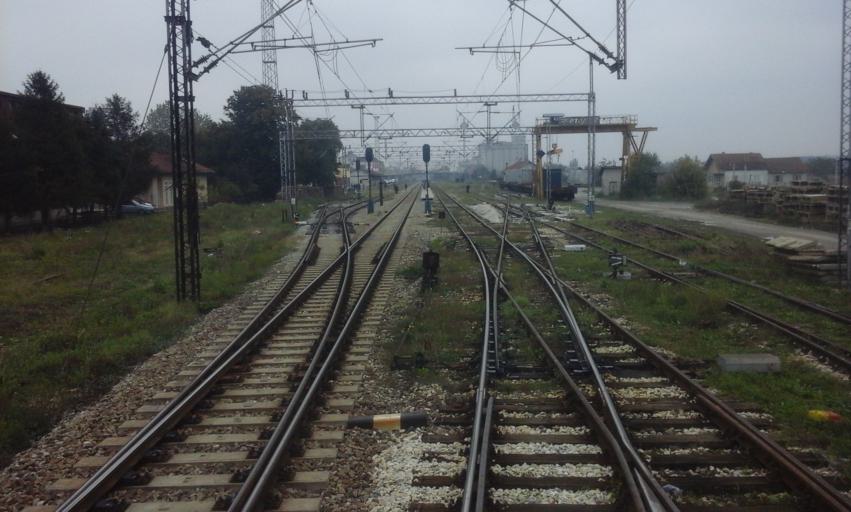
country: RS
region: Central Serbia
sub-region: Belgrade
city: Mladenovac
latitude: 44.4417
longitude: 20.6903
